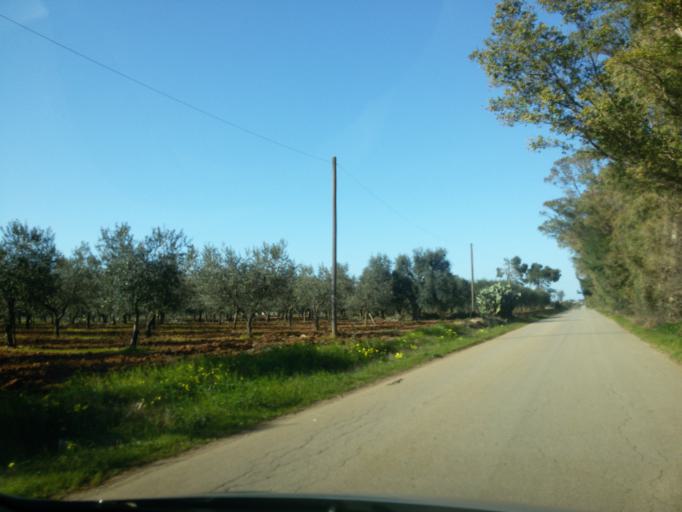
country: IT
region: Apulia
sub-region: Provincia di Brindisi
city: San Vito dei Normanni
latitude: 40.6732
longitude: 17.8206
